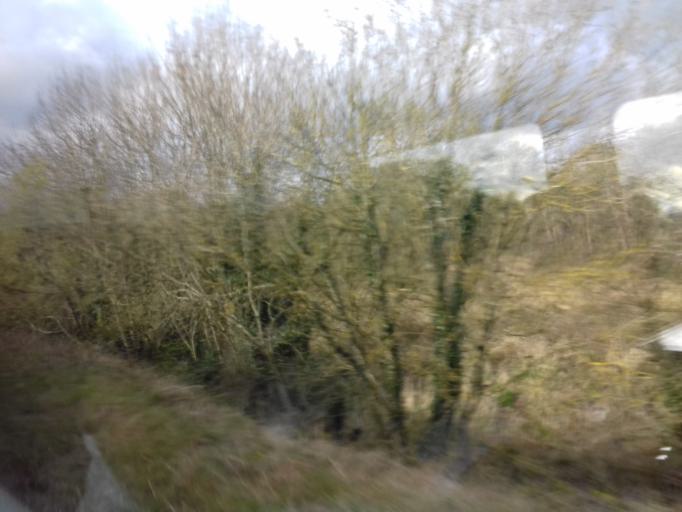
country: IE
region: Leinster
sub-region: An Iarmhi
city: An Muileann gCearr
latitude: 53.5097
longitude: -7.3163
